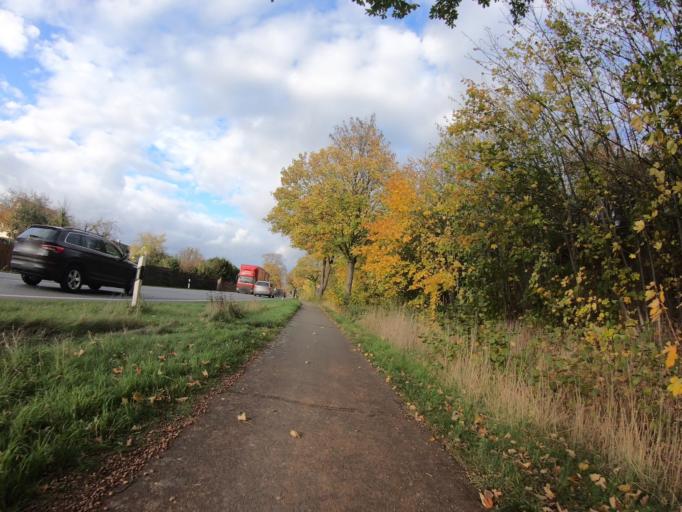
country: DE
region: Lower Saxony
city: Rotgesbuttel
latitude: 52.4187
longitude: 10.5346
